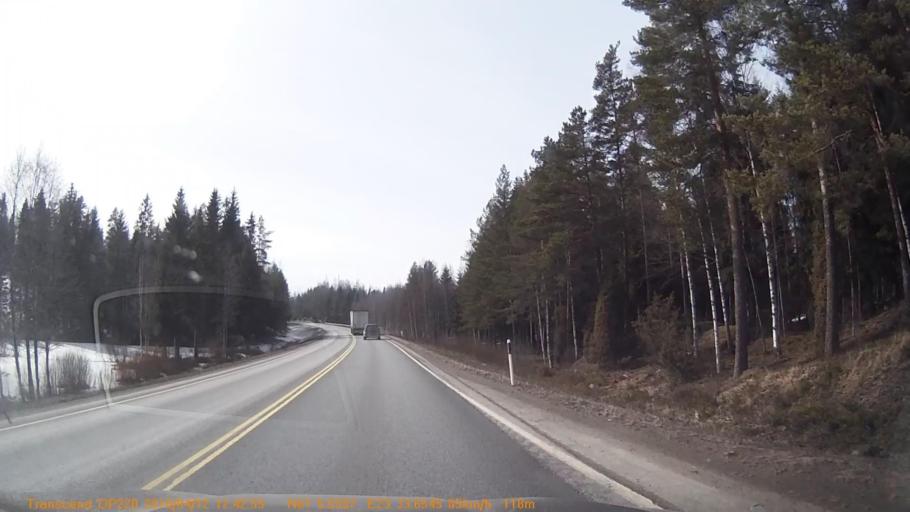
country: FI
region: Pirkanmaa
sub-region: Etelae-Pirkanmaa
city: Urjala
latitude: 61.0925
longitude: 23.5605
